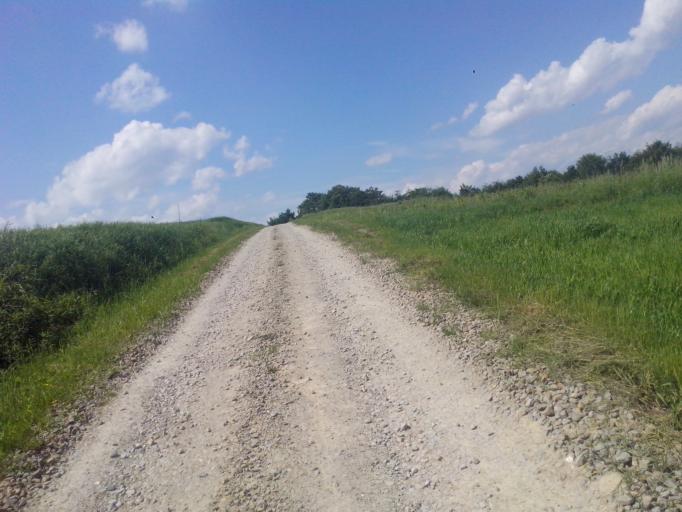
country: PL
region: Subcarpathian Voivodeship
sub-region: Powiat strzyzowski
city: Jawornik
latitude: 49.8403
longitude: 21.8549
